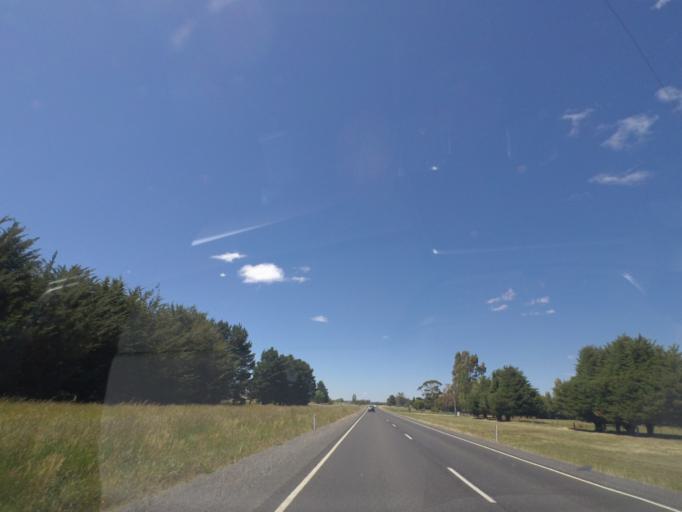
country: AU
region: Victoria
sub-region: Mount Alexander
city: Castlemaine
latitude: -37.2288
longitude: 144.3347
